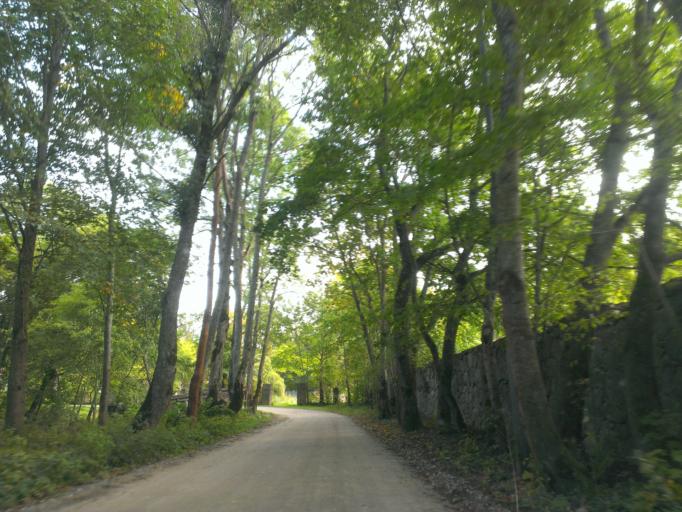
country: LV
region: Sigulda
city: Sigulda
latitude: 57.1696
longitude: 24.8273
